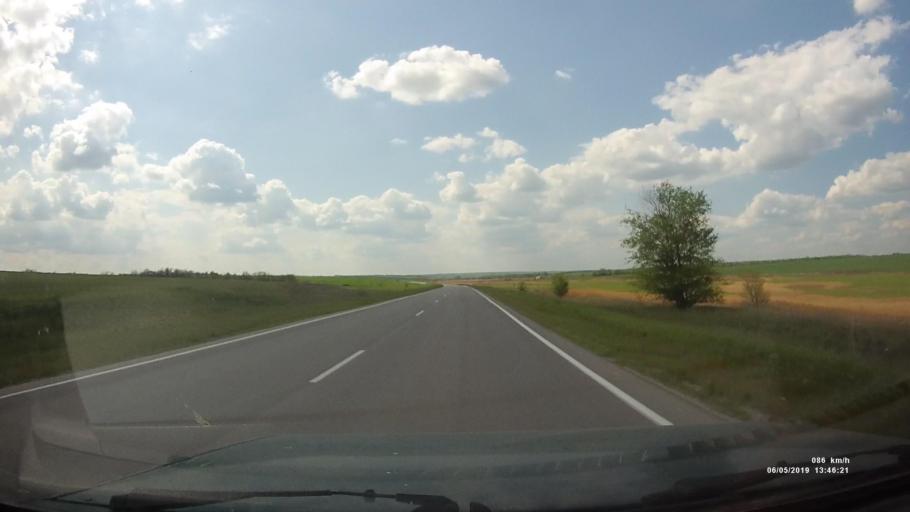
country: RU
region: Rostov
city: Melikhovskaya
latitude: 47.6587
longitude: 40.5815
